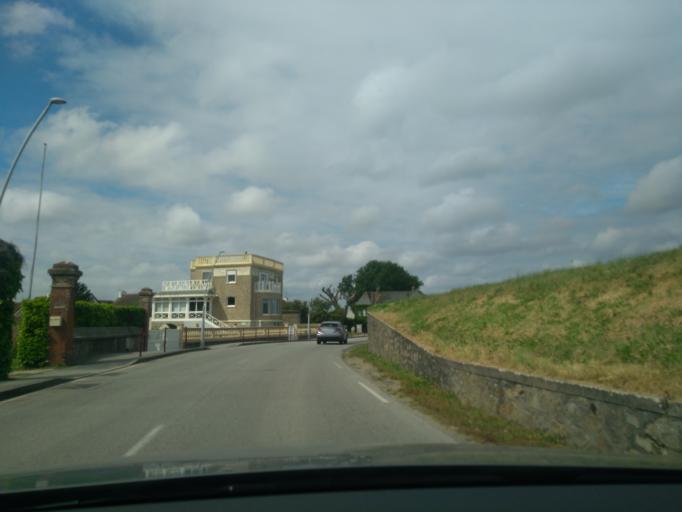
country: FR
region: Lower Normandy
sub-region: Departement de la Manche
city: Saint-Vaast-la-Hougue
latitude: 49.5925
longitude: -1.2668
